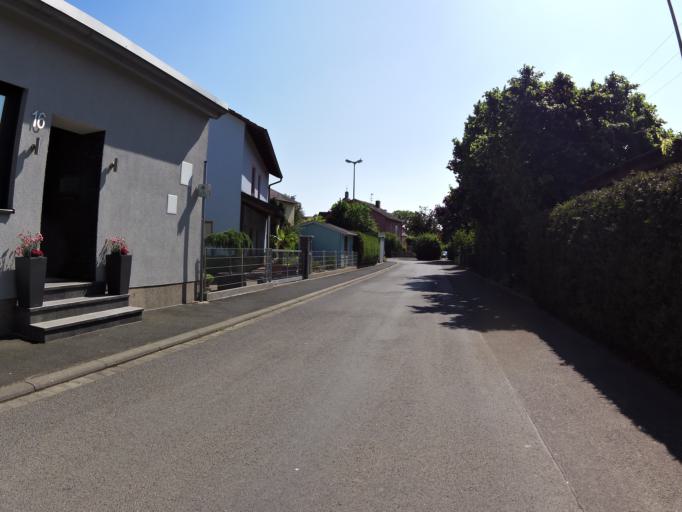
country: DE
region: Bavaria
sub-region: Regierungsbezirk Unterfranken
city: Kleinrinderfeld
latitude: 49.7016
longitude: 9.8473
